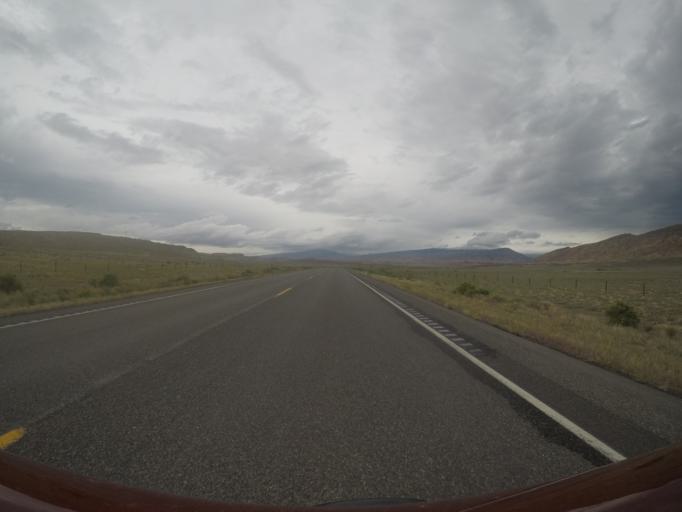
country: US
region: Wyoming
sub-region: Big Horn County
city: Lovell
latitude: 44.9225
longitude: -108.2976
